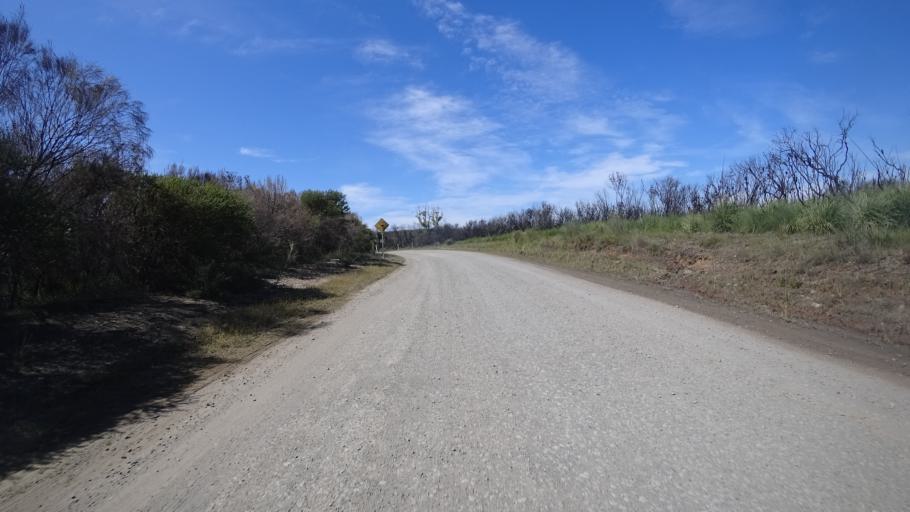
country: AU
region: New South Wales
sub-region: Shoalhaven Shire
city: Falls Creek
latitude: -35.1541
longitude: 150.7076
